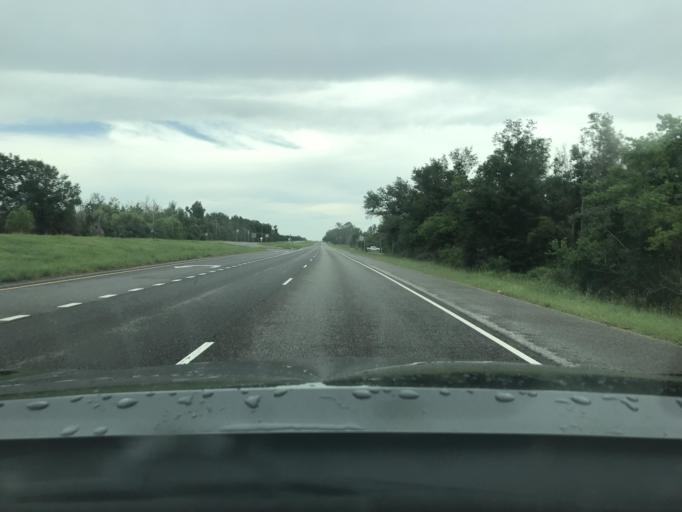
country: US
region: Louisiana
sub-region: Calcasieu Parish
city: Moss Bluff
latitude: 30.3963
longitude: -93.2301
